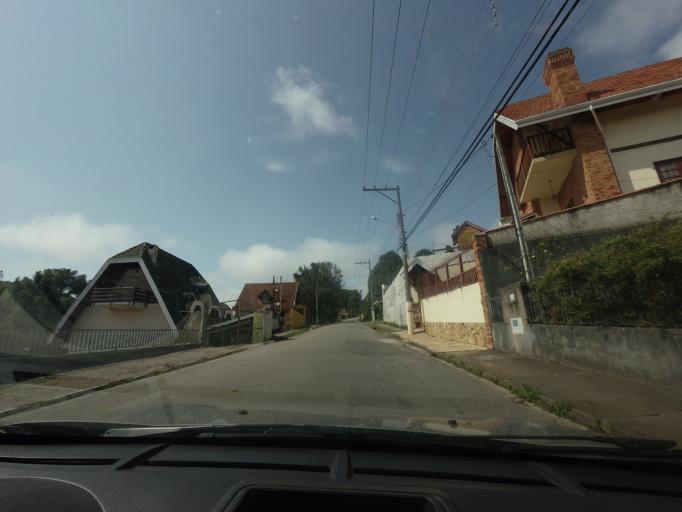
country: BR
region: Sao Paulo
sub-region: Campos Do Jordao
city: Campos do Jordao
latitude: -22.7481
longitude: -45.6029
